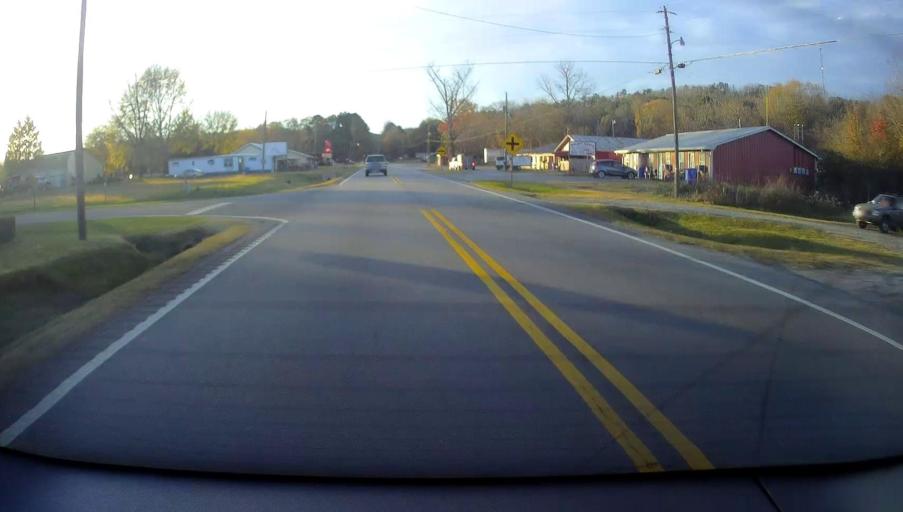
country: US
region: Alabama
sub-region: Saint Clair County
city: Steele
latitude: 34.0674
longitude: -86.3028
